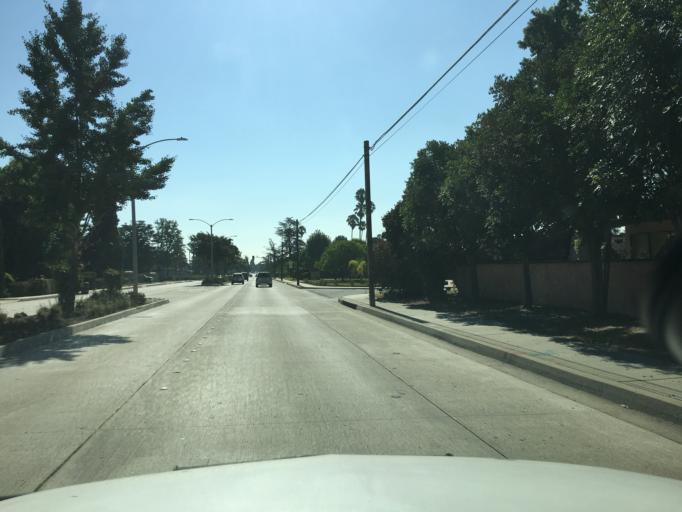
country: US
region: California
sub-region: Los Angeles County
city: Temple City
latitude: 34.1076
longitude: -118.0448
